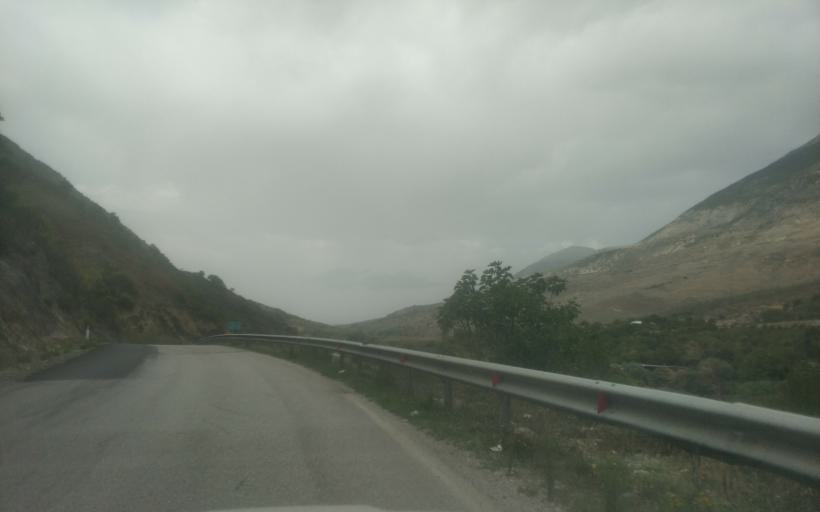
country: AL
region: Gjirokaster
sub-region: Rrethi i Gjirokastres
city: Picar
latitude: 40.2292
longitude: 20.0849
